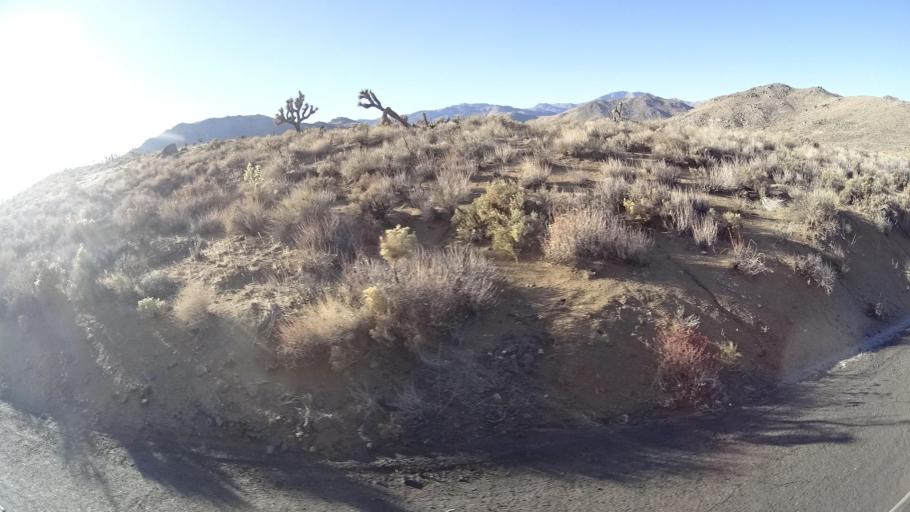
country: US
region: California
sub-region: Kern County
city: Weldon
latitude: 35.5218
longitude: -118.2025
